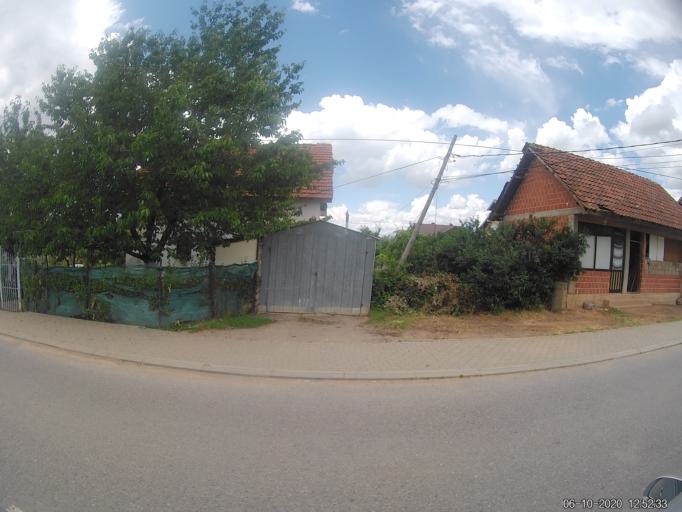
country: XK
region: Prizren
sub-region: Prizren
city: Prizren
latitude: 42.2328
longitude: 20.7616
